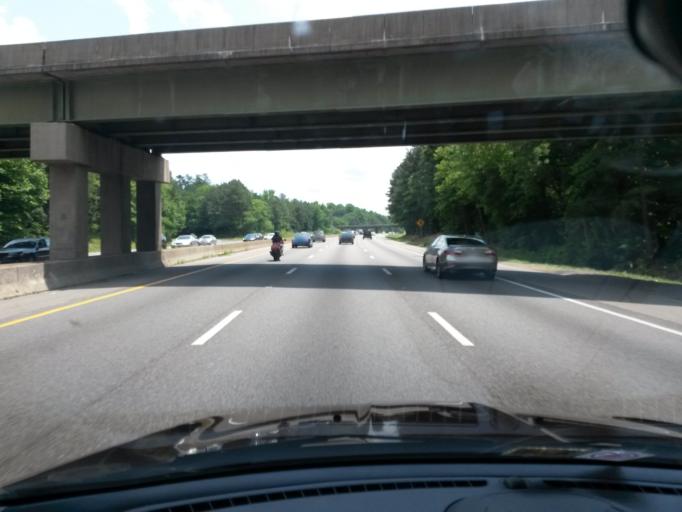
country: US
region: Virginia
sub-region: Chesterfield County
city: Chester
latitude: 37.3776
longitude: -77.4086
